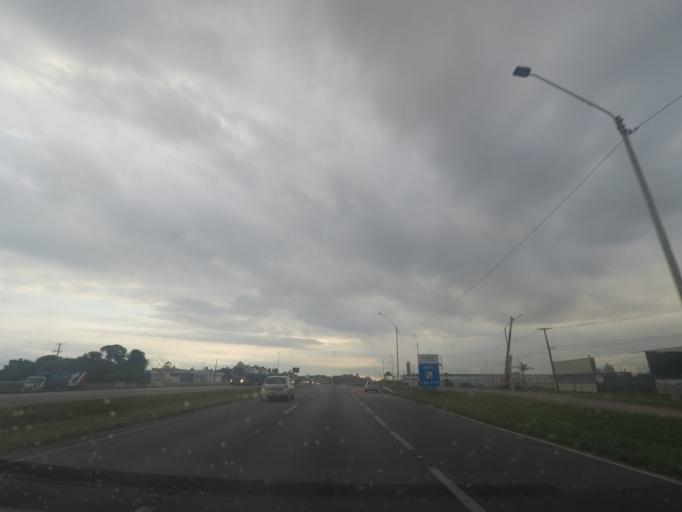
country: BR
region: Parana
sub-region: Sao Jose Dos Pinhais
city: Sao Jose dos Pinhais
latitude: -25.5714
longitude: -49.1954
